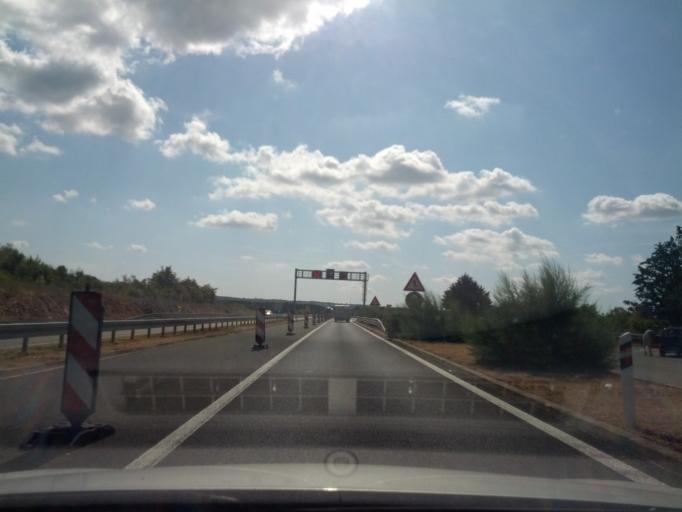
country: HR
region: Istarska
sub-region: Grad Rovinj
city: Rovinj
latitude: 45.1227
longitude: 13.7926
